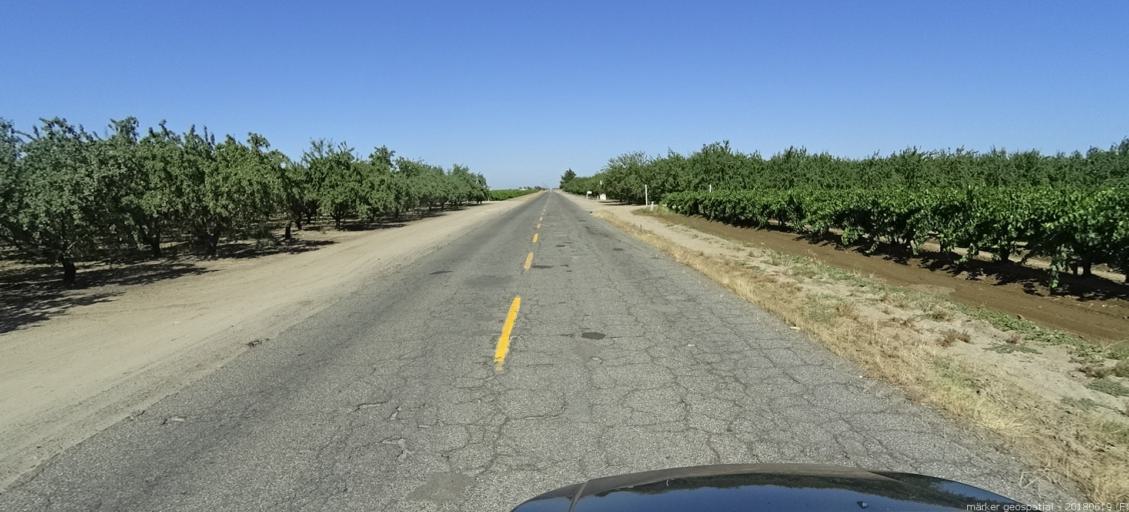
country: US
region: California
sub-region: Fresno County
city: Biola
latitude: 36.8368
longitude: -120.0597
